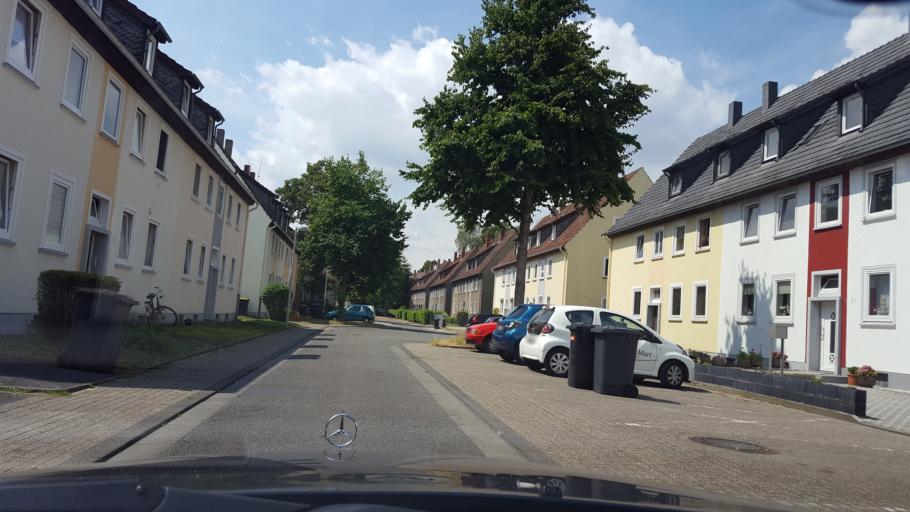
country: DE
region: North Rhine-Westphalia
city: Marl
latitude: 51.6680
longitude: 7.1215
